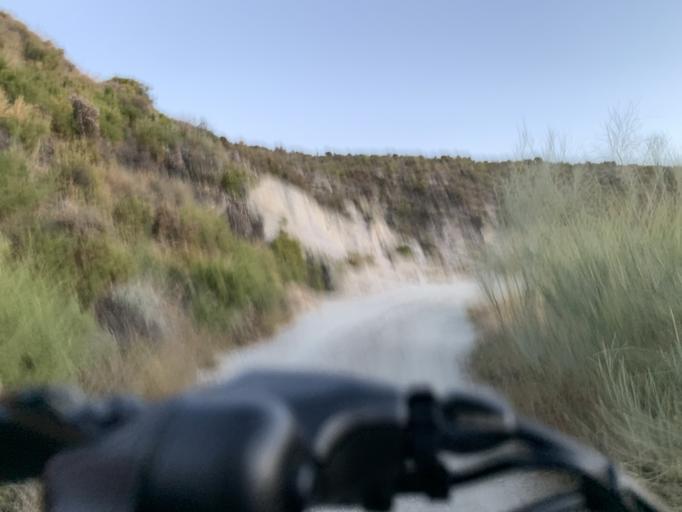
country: ES
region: Andalusia
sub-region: Provincia de Granada
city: Beas de Granada
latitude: 37.2250
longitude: -3.4597
